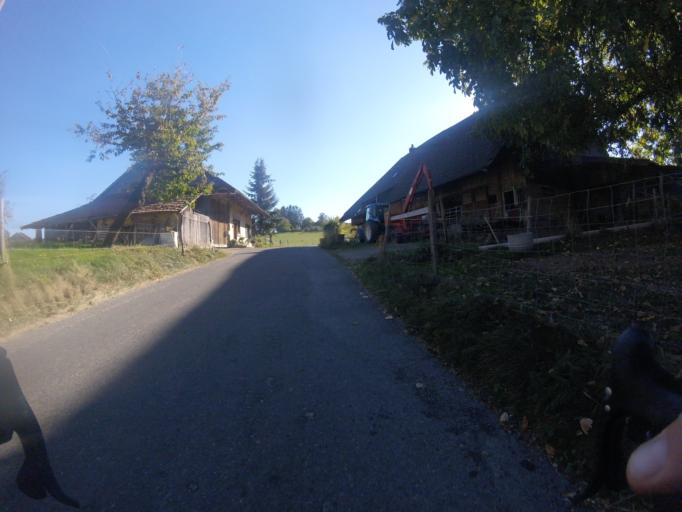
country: CH
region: Bern
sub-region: Seeland District
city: Schupfen
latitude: 47.0267
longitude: 7.3939
